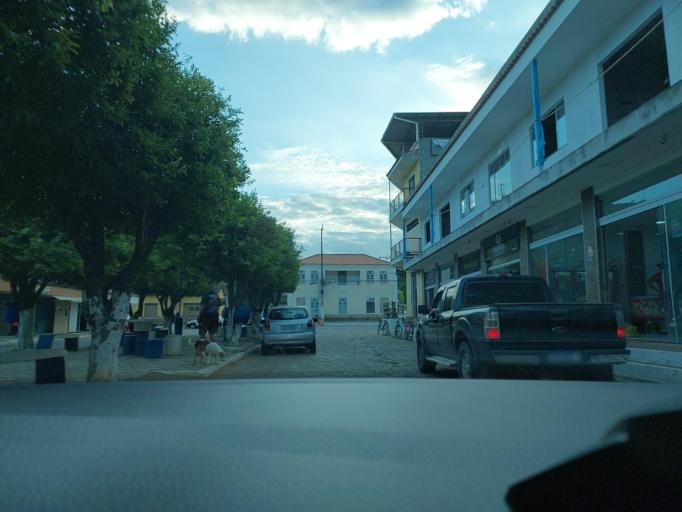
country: BR
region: Rio de Janeiro
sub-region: Natividade
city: Natividade
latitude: -21.1792
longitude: -42.1041
